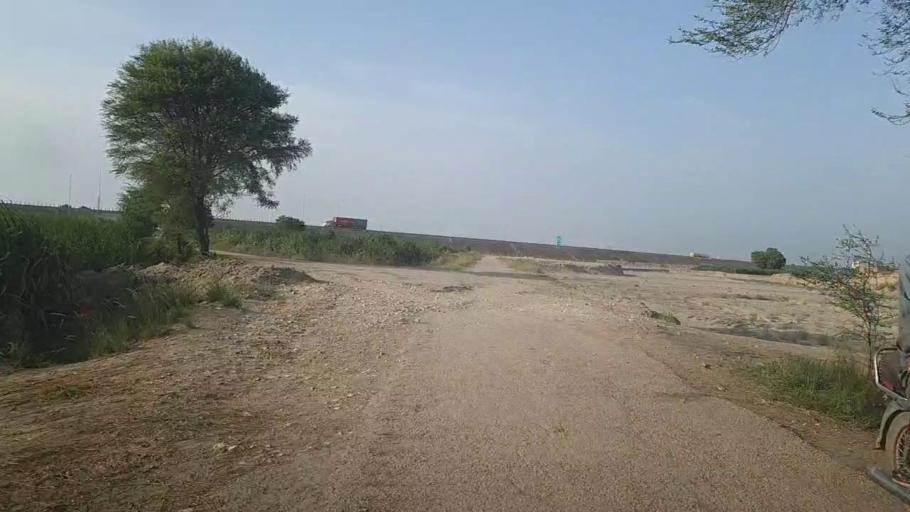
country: PK
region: Sindh
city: Ubauro
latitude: 28.3311
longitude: 69.7983
